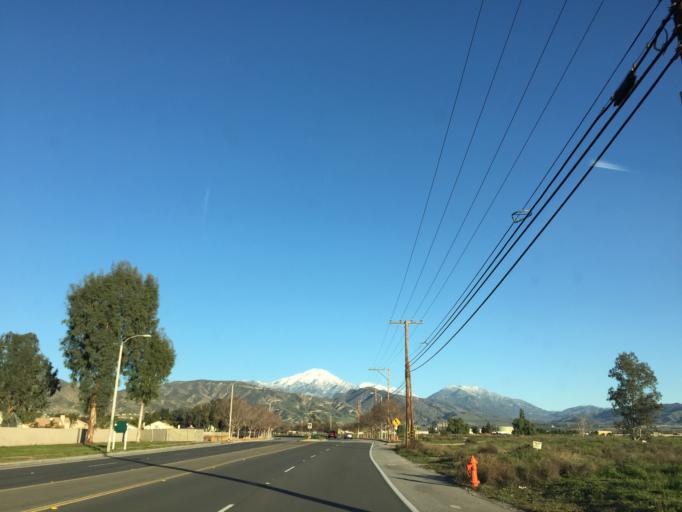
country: US
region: California
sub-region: San Bernardino County
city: Highland
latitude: 34.1083
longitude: -117.1792
